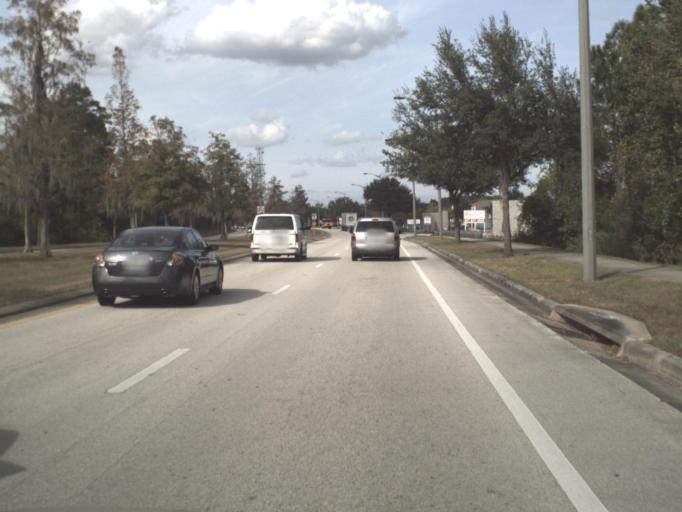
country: US
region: Florida
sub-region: Orange County
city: Taft
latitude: 28.4091
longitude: -81.2432
